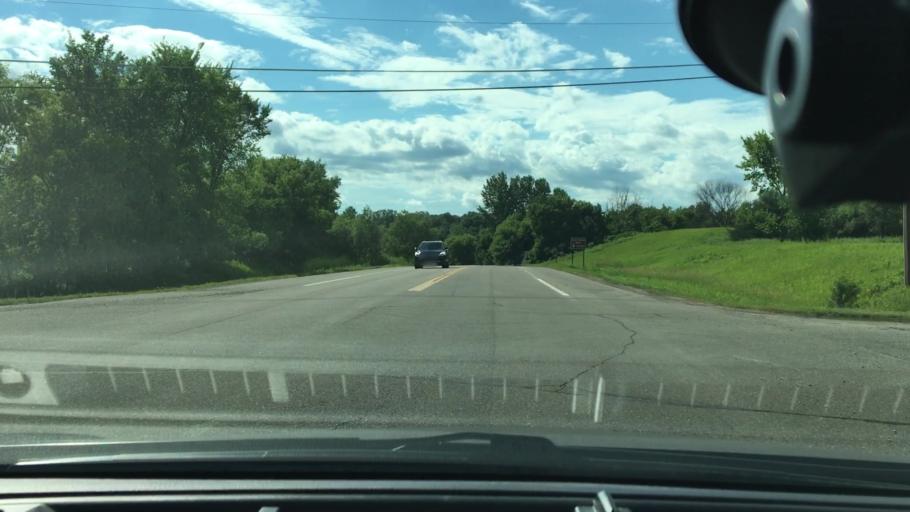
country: US
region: Minnesota
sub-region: Hennepin County
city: Minnetrista
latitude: 44.9235
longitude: -93.7013
